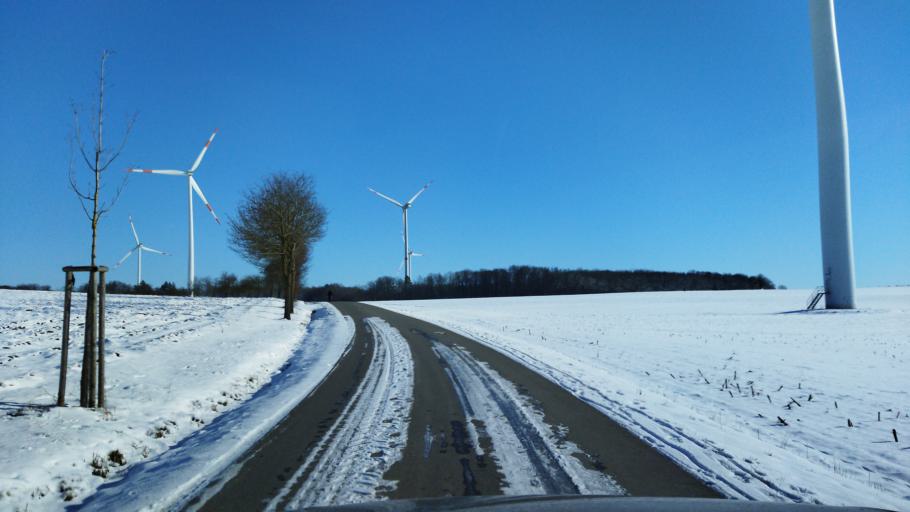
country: DE
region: Baden-Wuerttemberg
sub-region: Regierungsbezirk Stuttgart
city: Ilshofen
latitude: 49.1856
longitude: 9.9496
